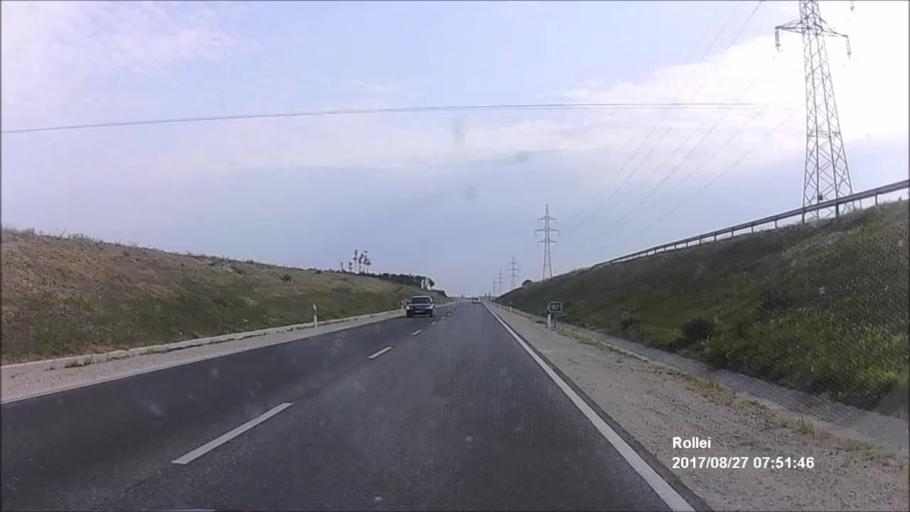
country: HU
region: Zala
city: Keszthely
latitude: 46.7697
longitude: 17.2170
